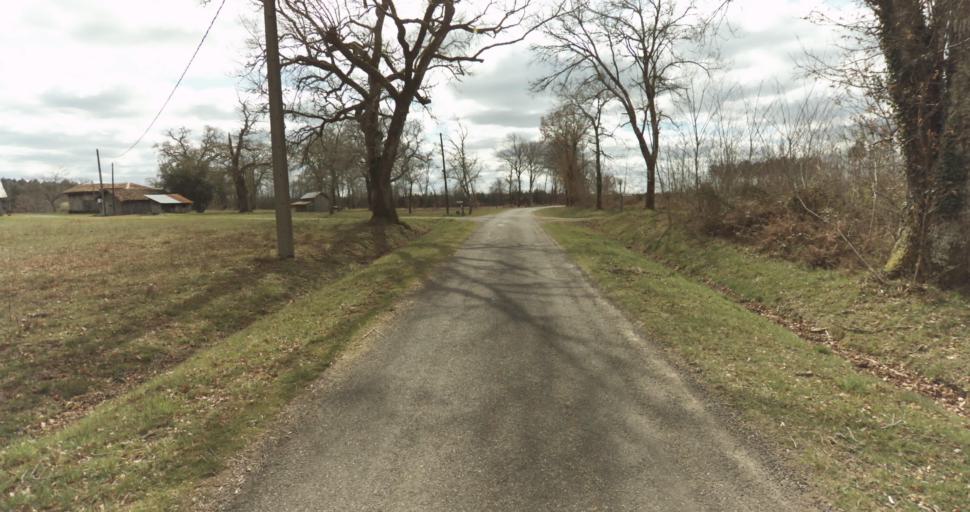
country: FR
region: Aquitaine
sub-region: Departement des Landes
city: Roquefort
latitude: 44.0662
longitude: -0.3981
